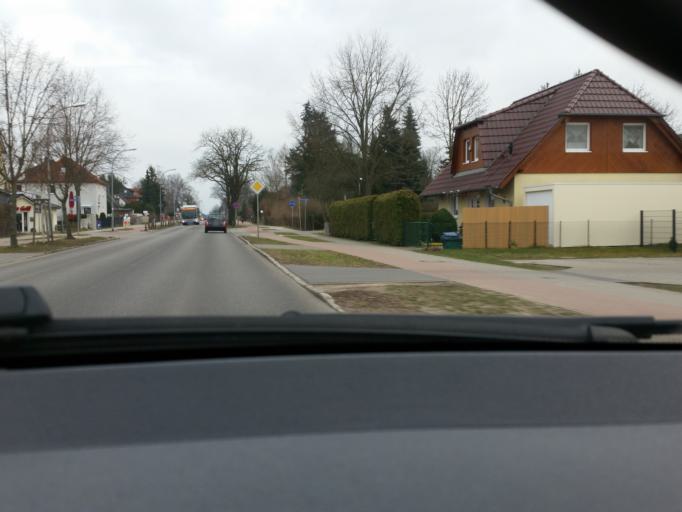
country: DE
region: Brandenburg
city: Teltow
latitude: 52.3930
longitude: 13.2882
